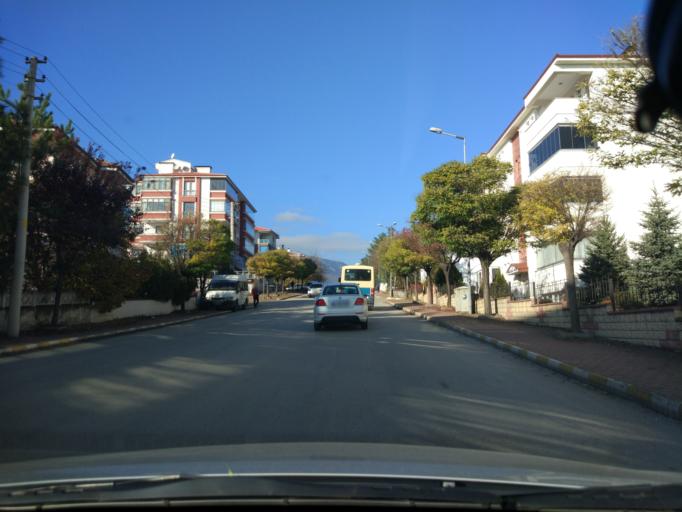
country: TR
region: Karabuk
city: Safranbolu
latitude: 41.2451
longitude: 32.6755
